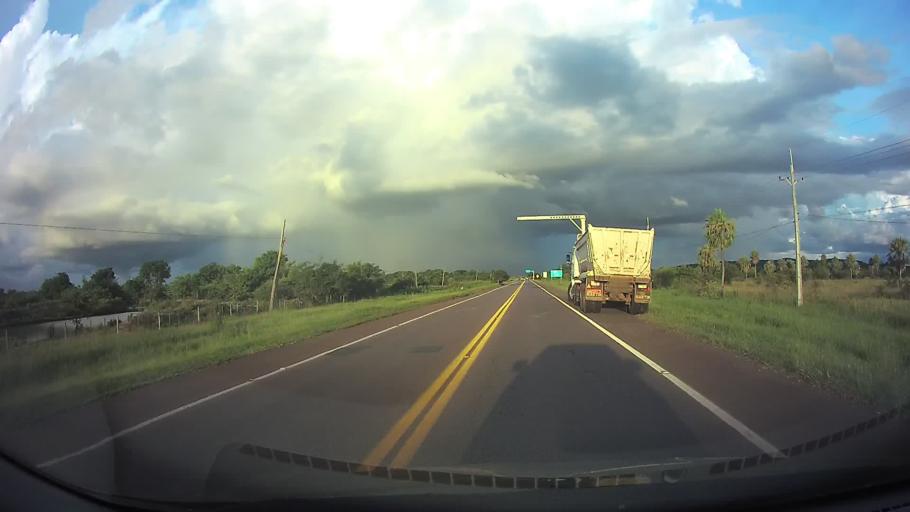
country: PY
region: Paraguari
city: Carapegua
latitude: -25.7522
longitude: -57.2233
